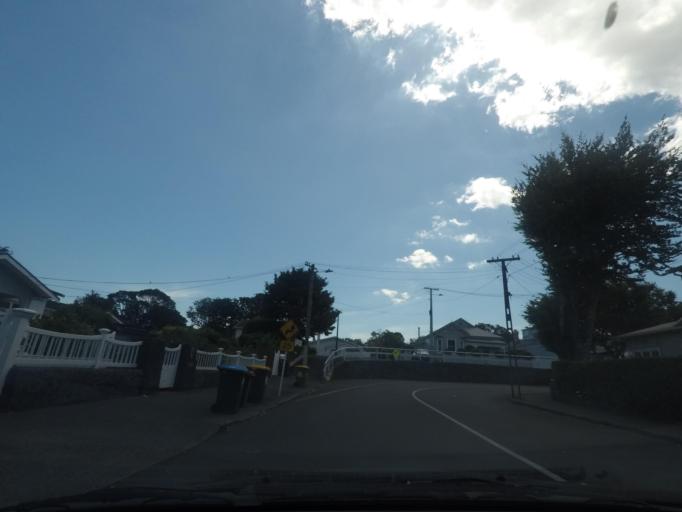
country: NZ
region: Auckland
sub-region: Auckland
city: Auckland
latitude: -36.8858
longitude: 174.7638
